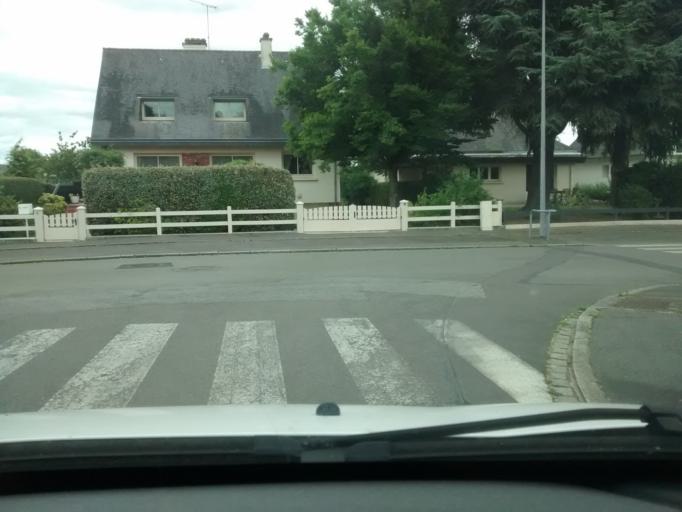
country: FR
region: Brittany
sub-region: Departement d'Ille-et-Vilaine
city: Cesson-Sevigne
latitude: 48.1191
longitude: -1.6118
